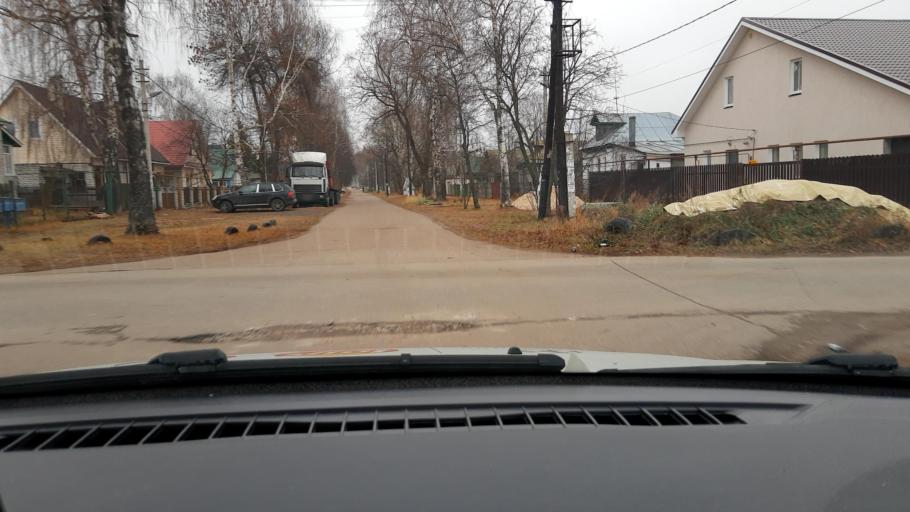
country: RU
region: Nizjnij Novgorod
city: Gorbatovka
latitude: 56.2040
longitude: 43.7673
